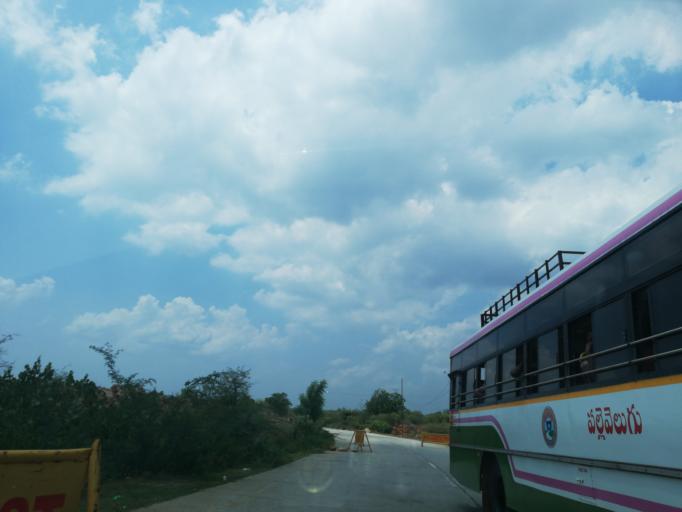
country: IN
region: Andhra Pradesh
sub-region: Guntur
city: Macherla
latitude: 16.5684
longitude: 79.3333
